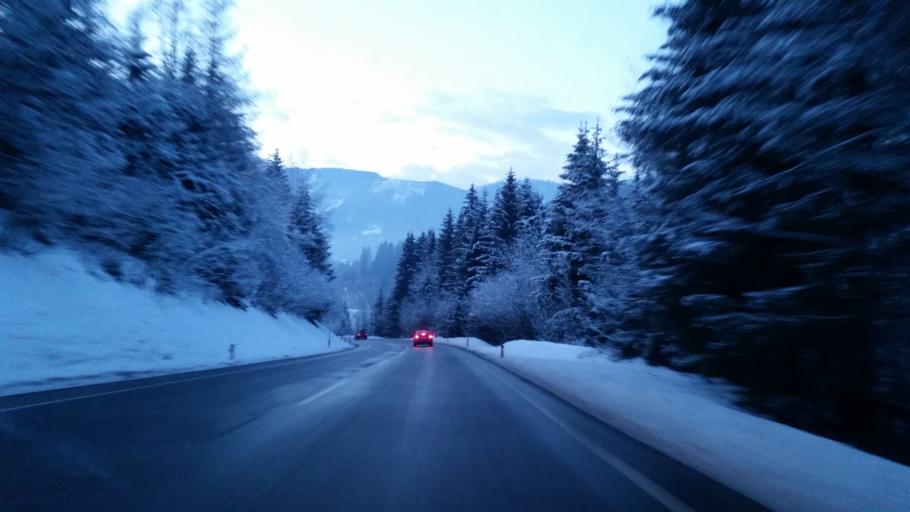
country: AT
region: Salzburg
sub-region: Politischer Bezirk Sankt Johann im Pongau
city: Eben im Pongau
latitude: 47.4170
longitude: 13.3806
